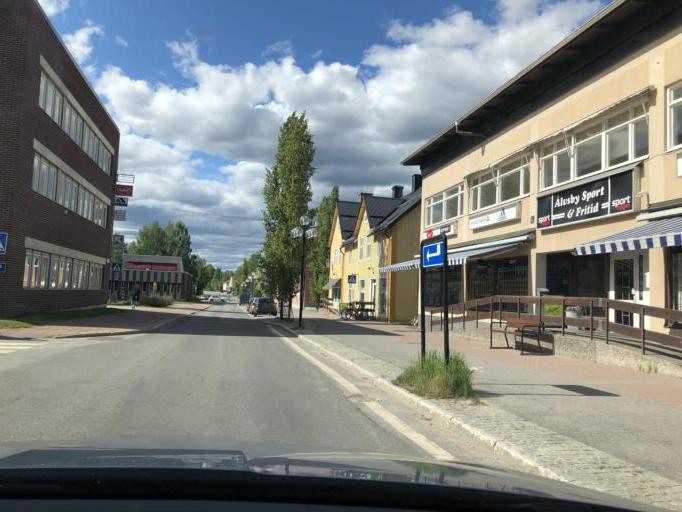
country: SE
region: Norrbotten
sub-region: Alvsbyns Kommun
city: AElvsbyn
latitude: 65.6738
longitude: 21.0082
